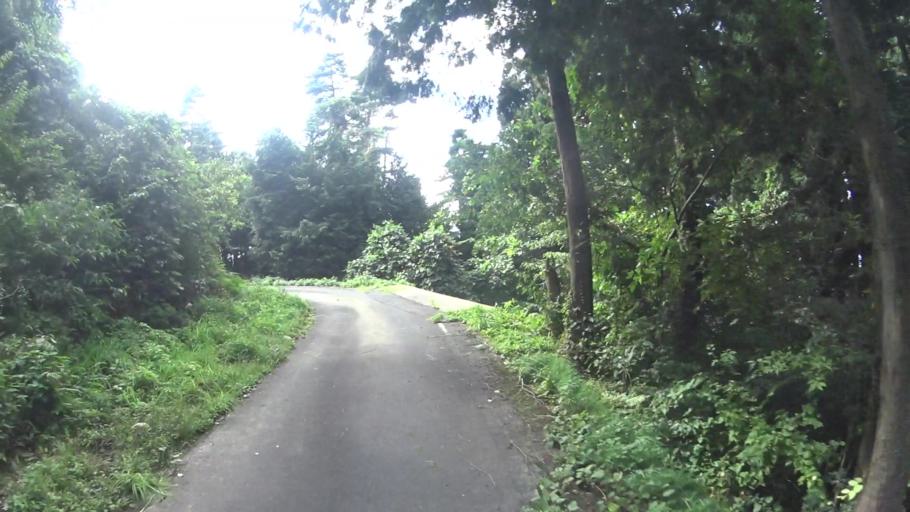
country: JP
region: Kyoto
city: Miyazu
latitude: 35.7364
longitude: 135.1963
